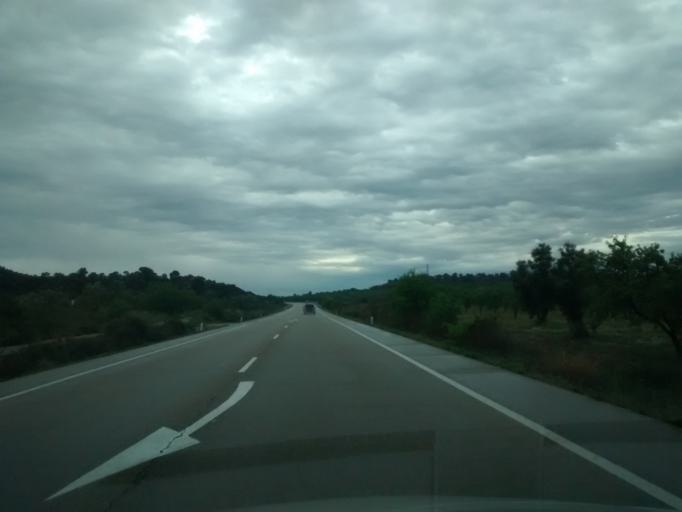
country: ES
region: Aragon
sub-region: Provincia de Zaragoza
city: Maella
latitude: 41.1448
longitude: 0.1132
